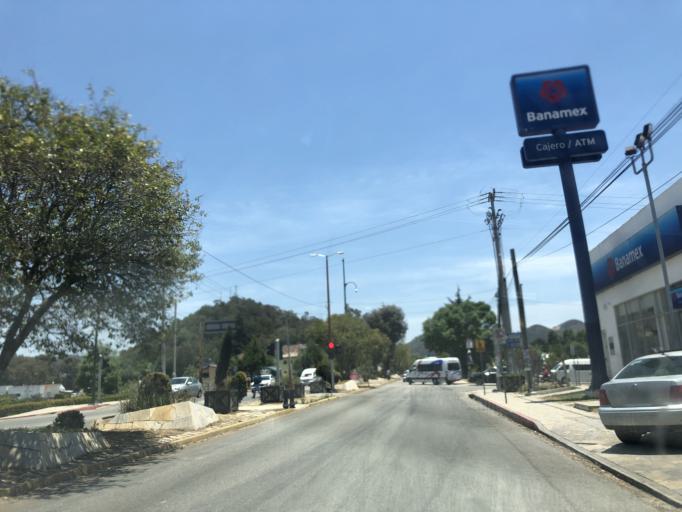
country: MX
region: Chiapas
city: San Cristobal de las Casas
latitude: 16.7322
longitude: -92.6514
